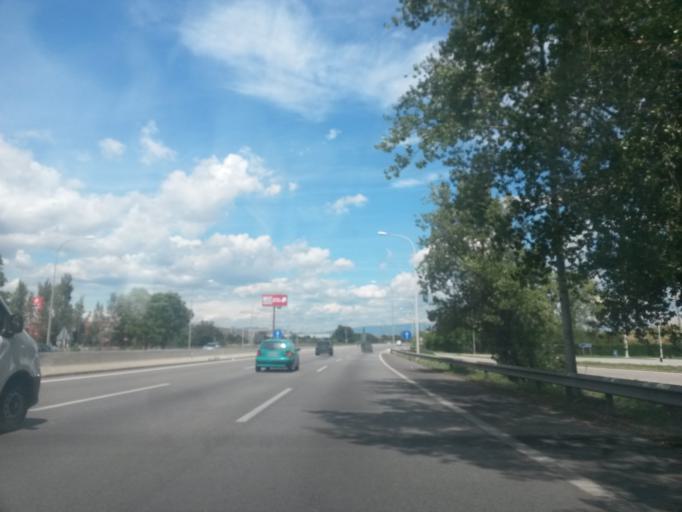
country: ES
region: Catalonia
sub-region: Provincia de Barcelona
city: Montcada i Reixac
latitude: 41.4962
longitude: 2.1913
